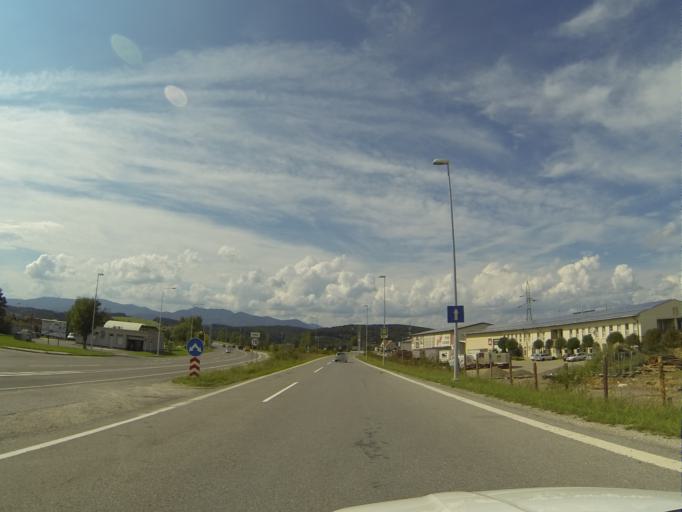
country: SK
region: Nitriansky
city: Novaky
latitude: 48.7237
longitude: 18.5552
